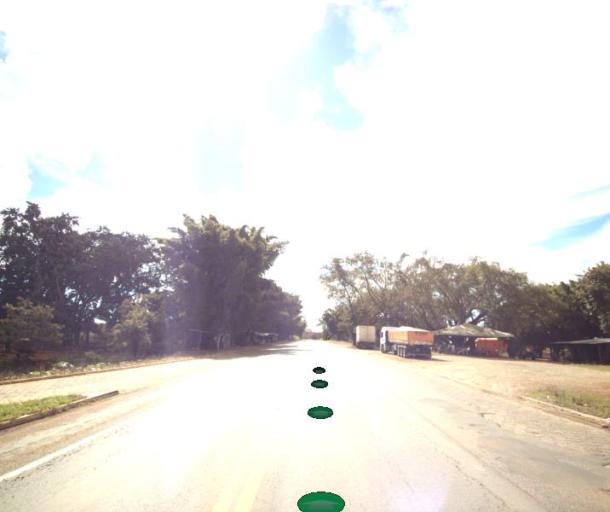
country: BR
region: Goias
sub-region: Jaragua
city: Jaragua
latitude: -15.8580
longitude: -49.2629
